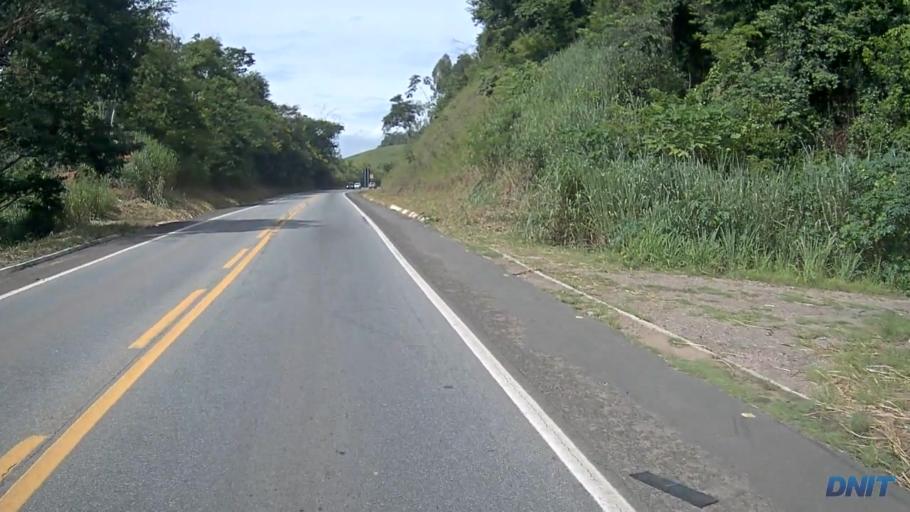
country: BR
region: Minas Gerais
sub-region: Ipatinga
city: Ipatinga
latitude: -19.4272
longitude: -42.5013
